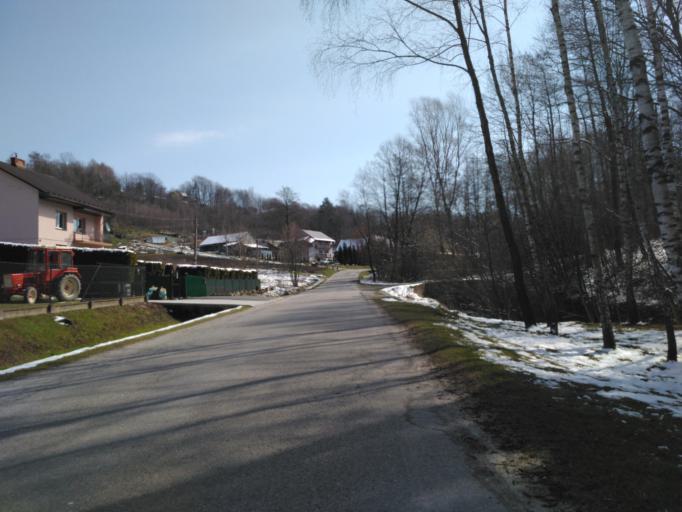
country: PL
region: Subcarpathian Voivodeship
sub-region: Powiat ropczycko-sedziszowski
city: Wielopole Skrzynskie
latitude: 49.9894
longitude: 21.5827
